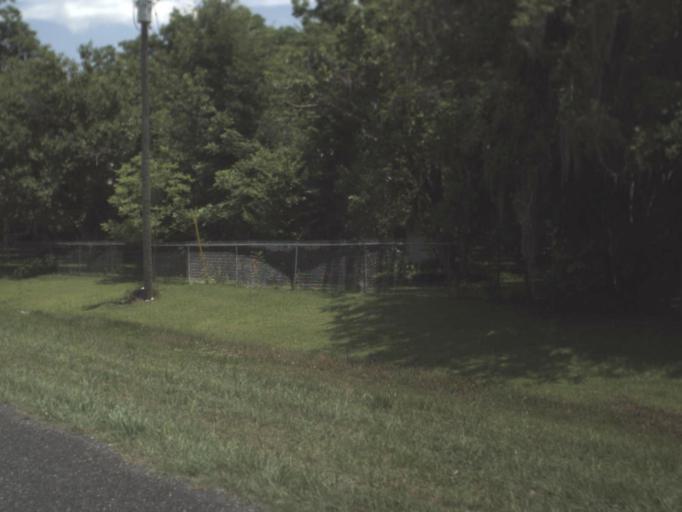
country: US
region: Florida
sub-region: Alachua County
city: Newberry
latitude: 29.6544
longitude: -82.5497
